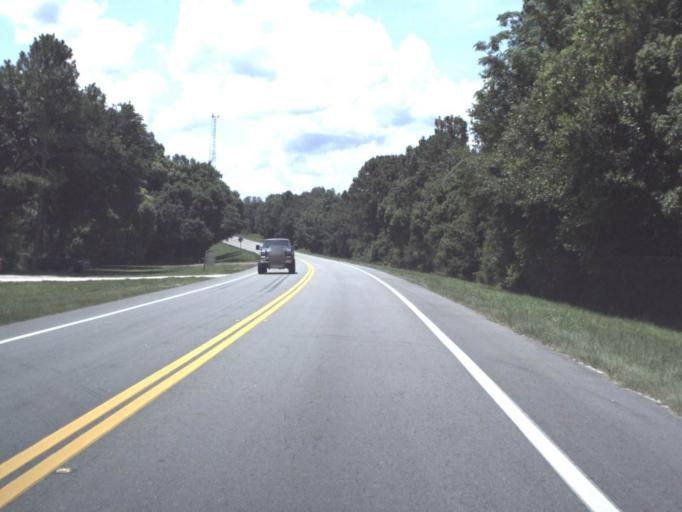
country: US
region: Florida
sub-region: Putnam County
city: Crescent City
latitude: 29.3697
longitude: -81.5093
